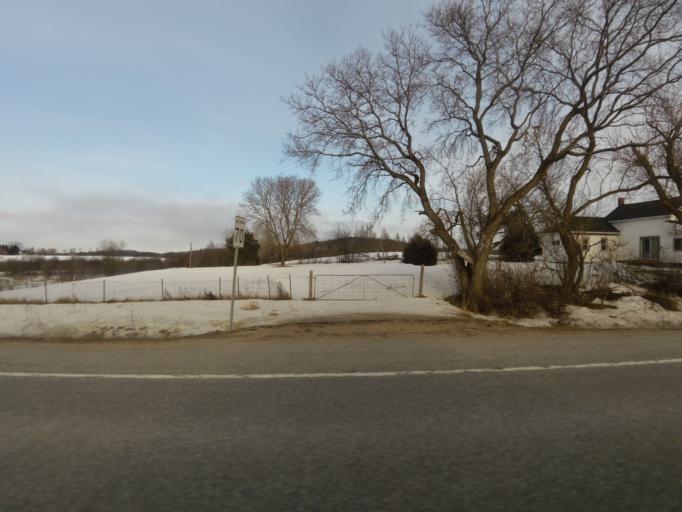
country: CA
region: Quebec
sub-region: Outaouais
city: Wakefield
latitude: 45.8655
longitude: -76.0217
